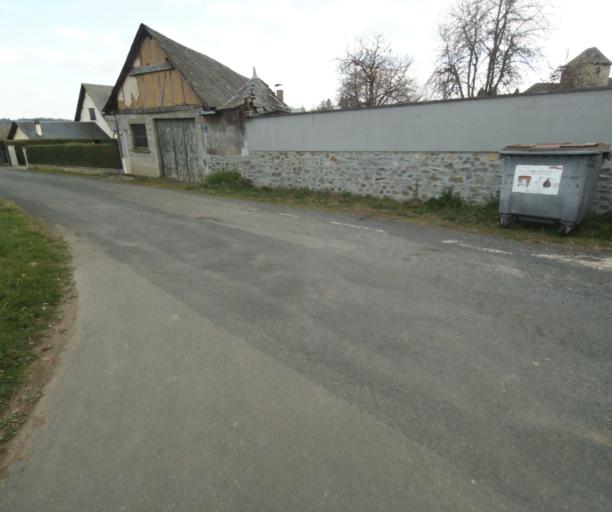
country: FR
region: Limousin
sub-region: Departement de la Correze
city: Saint-Clement
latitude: 45.3537
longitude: 1.6400
